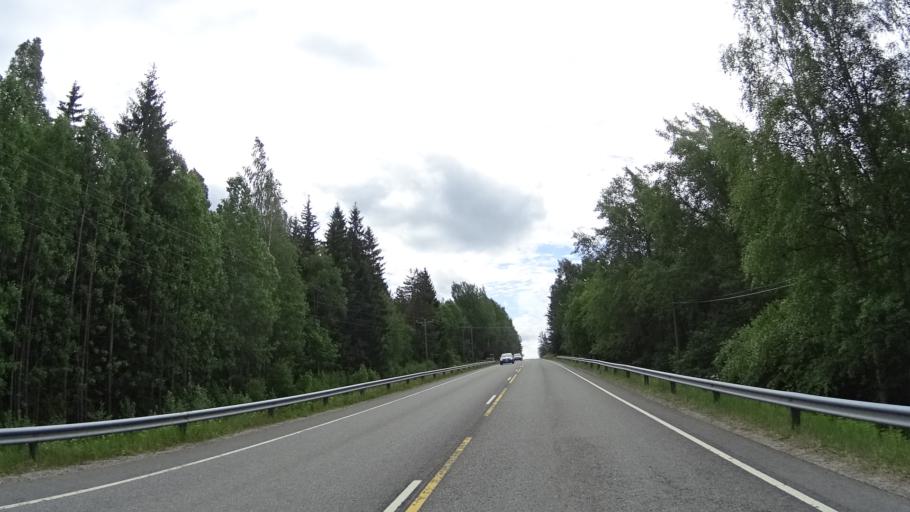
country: FI
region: Uusimaa
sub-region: Helsinki
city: Vihti
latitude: 60.2958
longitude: 24.3881
